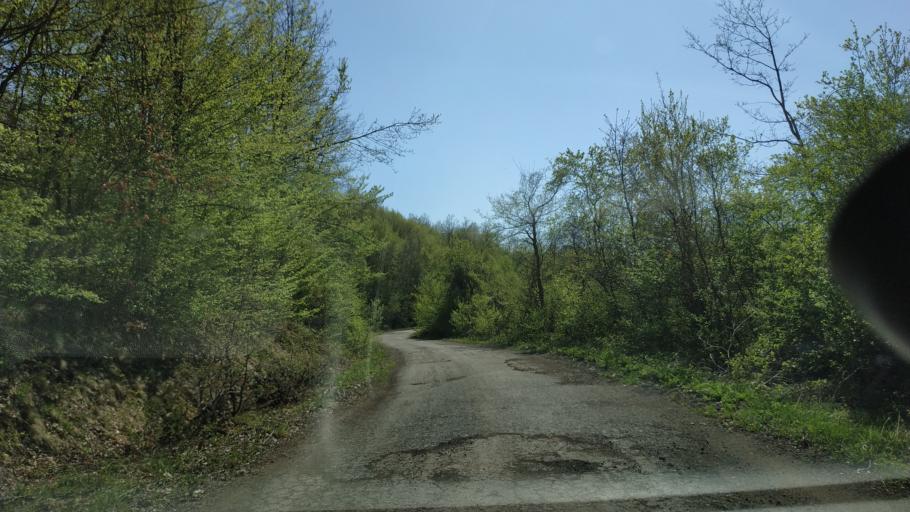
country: RS
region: Central Serbia
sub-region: Zajecarski Okrug
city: Soko Banja
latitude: 43.5076
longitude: 21.8991
